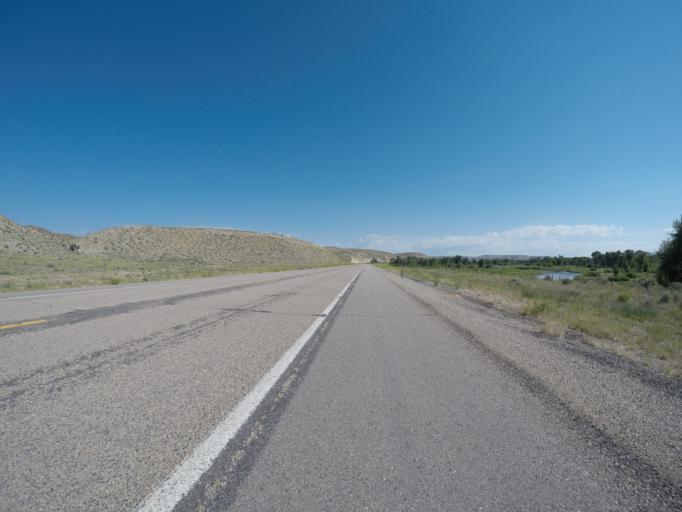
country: US
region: Wyoming
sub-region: Sublette County
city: Marbleton
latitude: 42.1681
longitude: -110.1887
